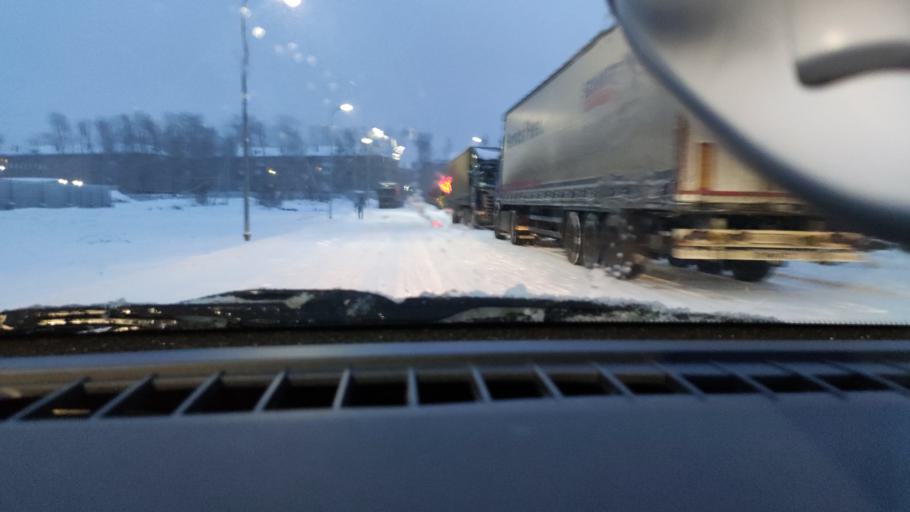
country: RU
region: Perm
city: Kondratovo
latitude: 57.9740
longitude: 56.1542
